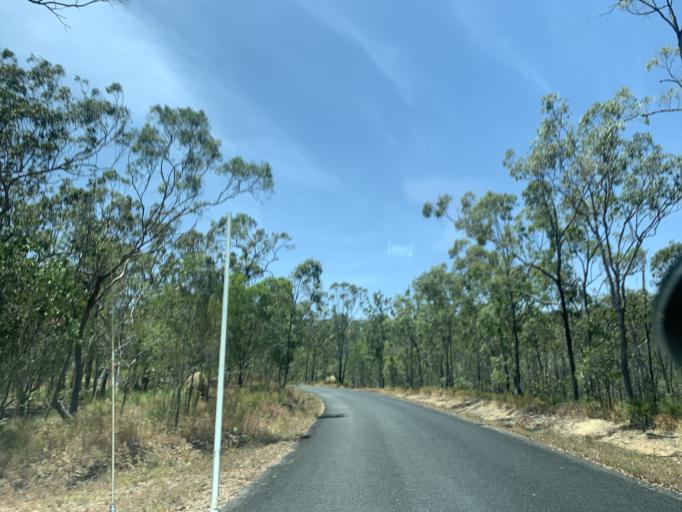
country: AU
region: Queensland
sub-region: Tablelands
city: Kuranda
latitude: -16.9178
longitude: 145.5823
